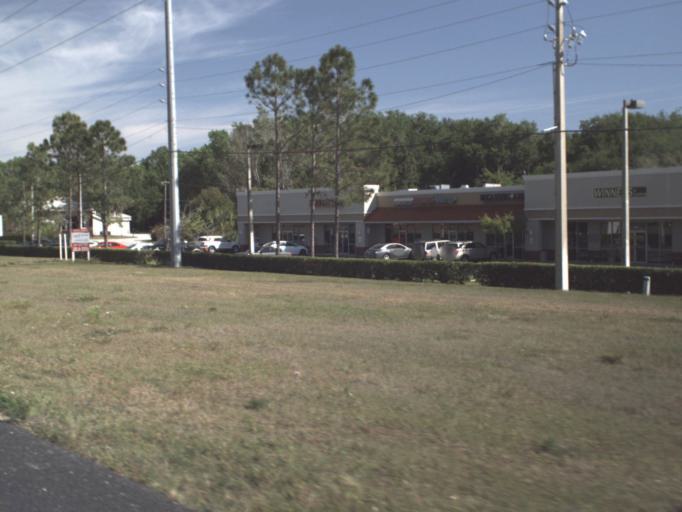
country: US
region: Florida
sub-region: Lake County
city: Hawthorne
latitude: 28.7731
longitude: -81.8857
